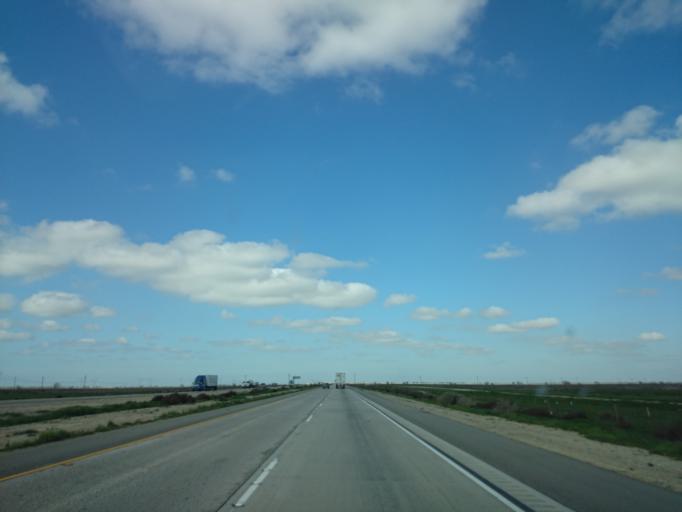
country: US
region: California
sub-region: Kern County
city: Rosedale
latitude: 35.3170
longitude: -119.2823
